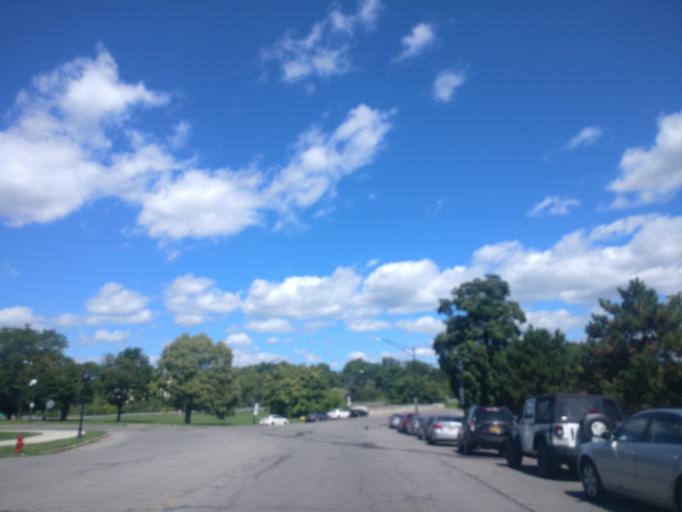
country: US
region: New York
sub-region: Erie County
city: Kenmore
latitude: 42.9325
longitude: -78.8745
